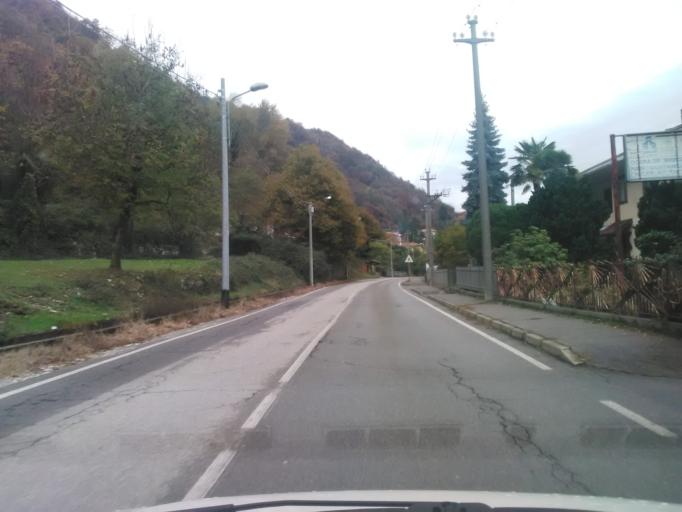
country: IT
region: Piedmont
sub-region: Provincia Verbano-Cusio-Ossola
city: Madonna del Sasso
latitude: 45.7905
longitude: 8.3779
